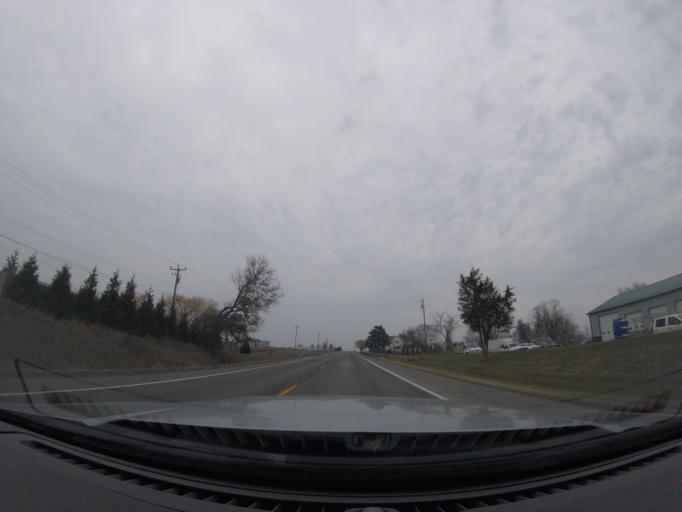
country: US
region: New York
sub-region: Yates County
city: Dundee
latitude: 42.6266
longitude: -76.9437
